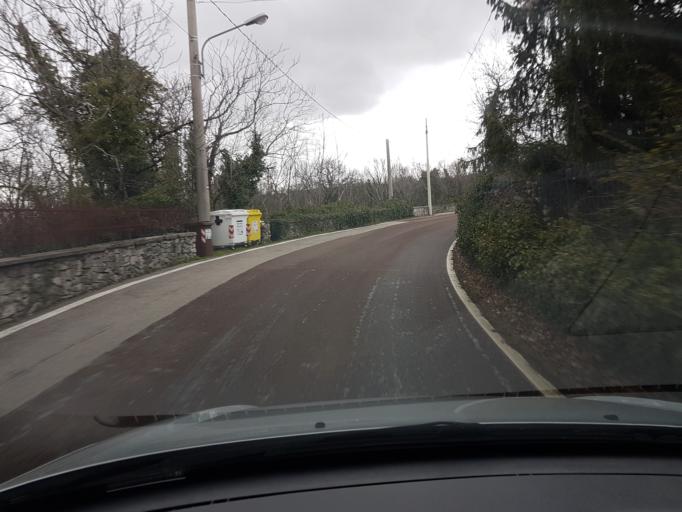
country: IT
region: Friuli Venezia Giulia
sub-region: Provincia di Trieste
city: Sgonico
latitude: 45.7298
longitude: 13.7300
